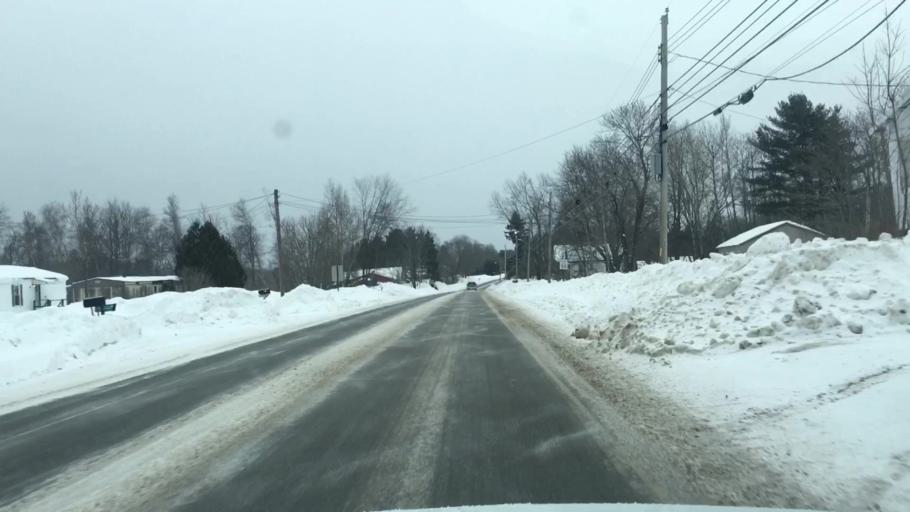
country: US
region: Maine
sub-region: Penobscot County
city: Lincoln
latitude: 45.3990
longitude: -68.4915
